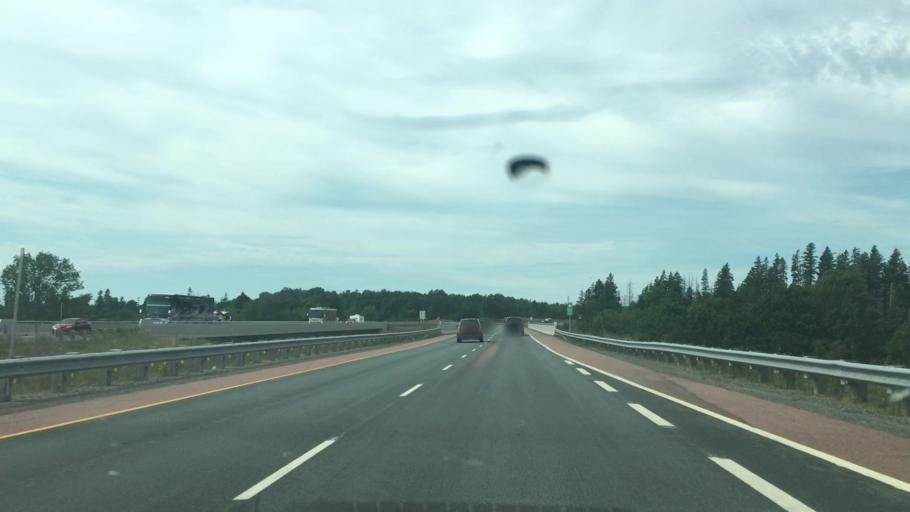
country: CA
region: Nova Scotia
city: Antigonish
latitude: 45.6093
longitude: -61.9789
